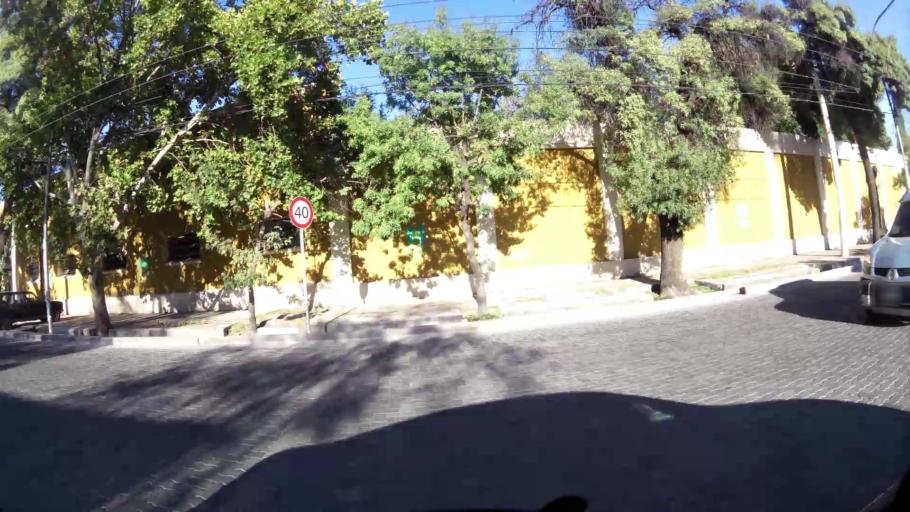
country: AR
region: Mendoza
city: Las Heras
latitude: -32.8565
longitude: -68.8336
